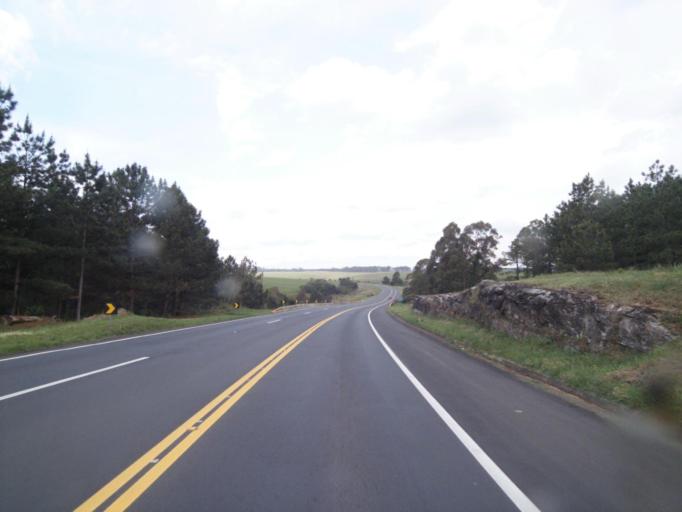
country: BR
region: Parana
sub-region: Palmeira
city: Palmeira
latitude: -25.4690
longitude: -49.7807
